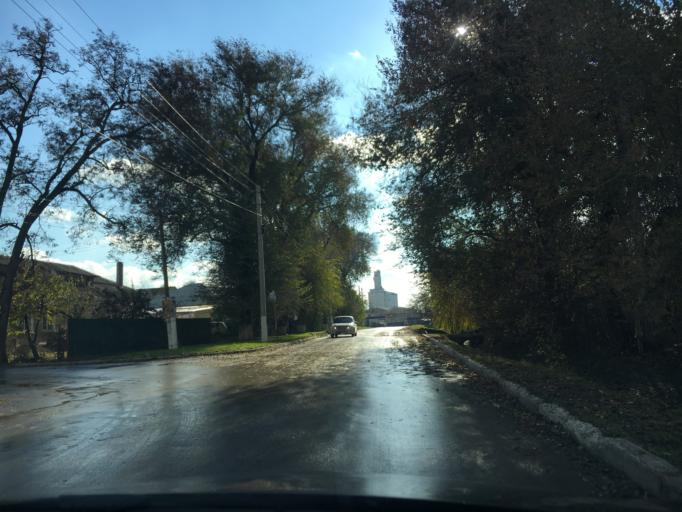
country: RU
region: Rostov
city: Matveyev Kurgan
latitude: 47.5637
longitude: 38.8615
